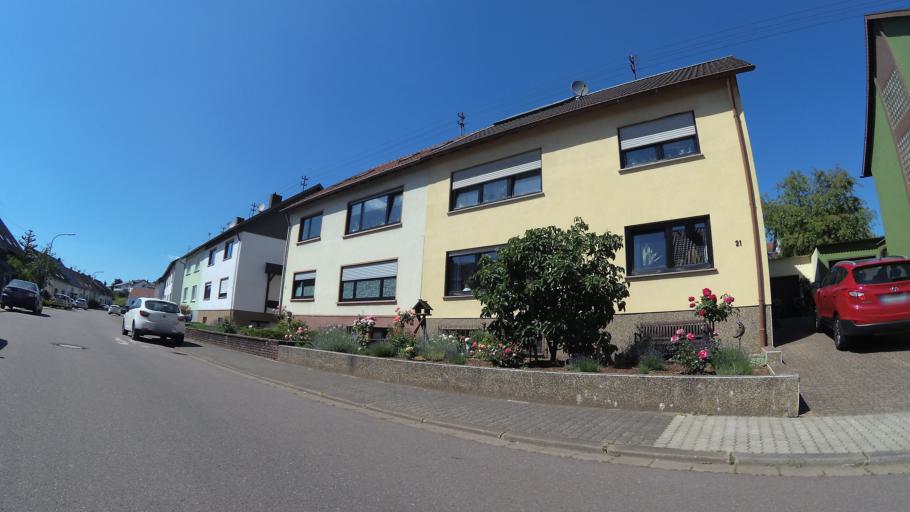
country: DE
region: Saarland
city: Saarwellingen
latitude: 49.3524
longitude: 6.8000
